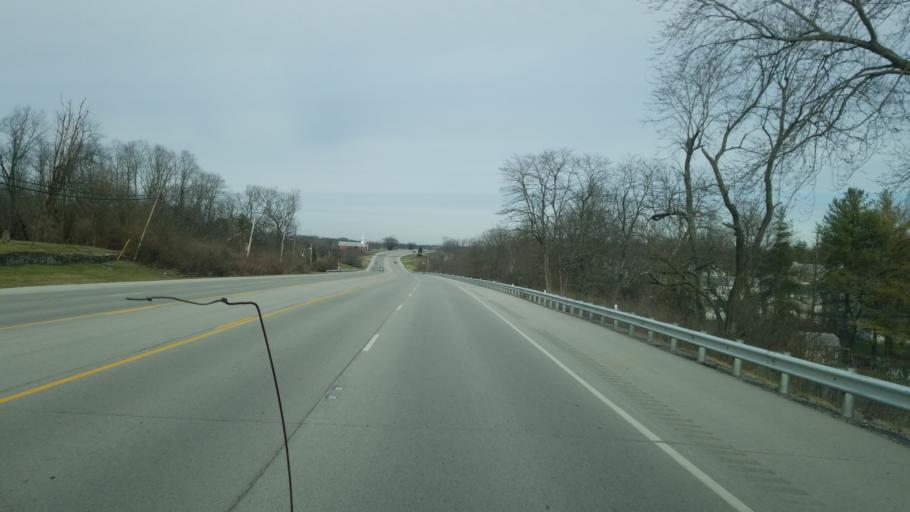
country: US
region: Ohio
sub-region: Brown County
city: Aberdeen
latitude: 38.6136
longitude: -83.8100
